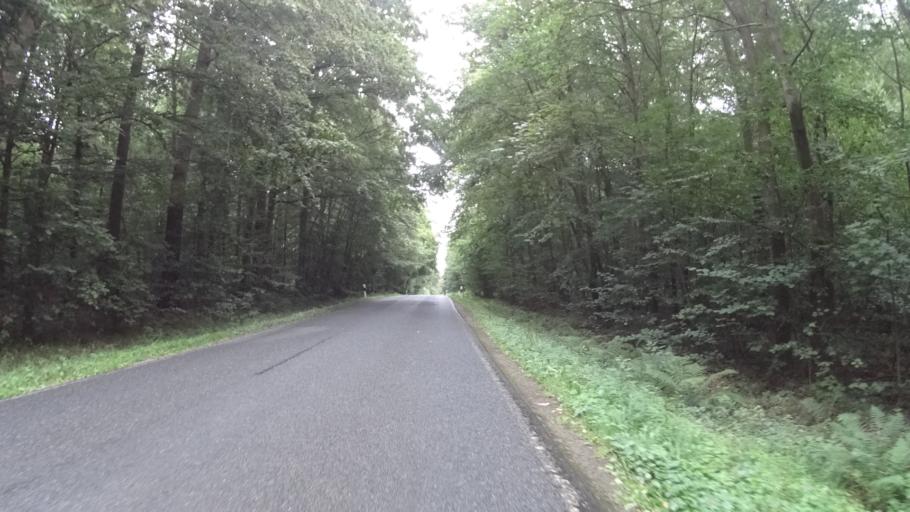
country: DE
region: Schleswig-Holstein
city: Nusse
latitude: 53.6850
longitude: 10.5936
